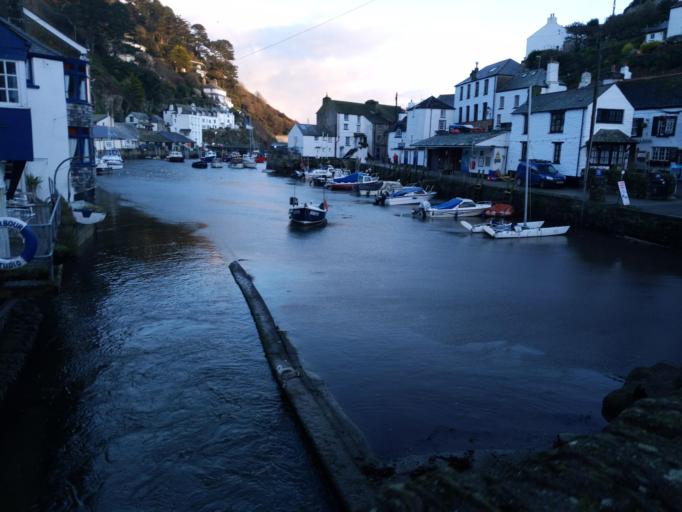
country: GB
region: England
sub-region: Cornwall
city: Duloe
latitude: 50.3314
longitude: -4.5183
